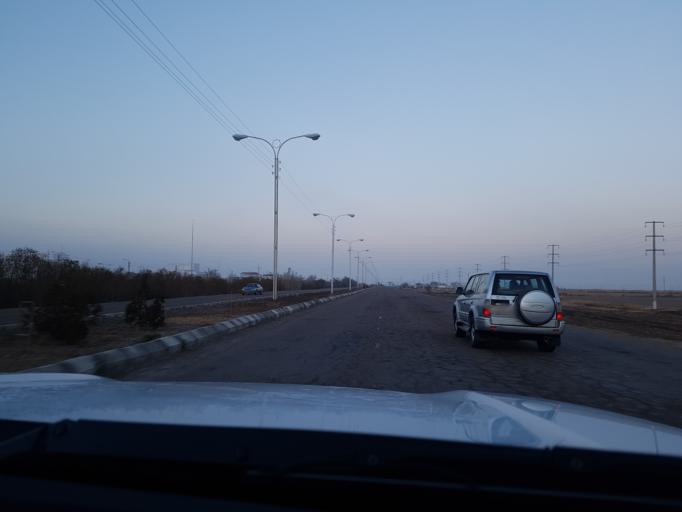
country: TM
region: Dasoguz
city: Koeneuergench
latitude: 41.7429
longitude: 58.6979
